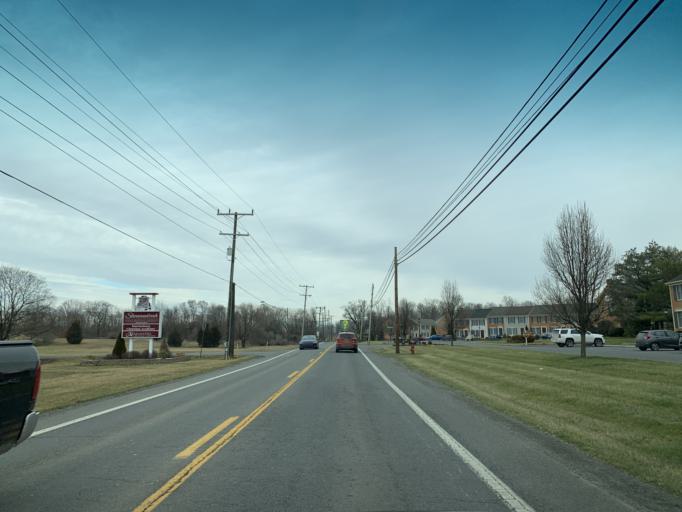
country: US
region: West Virginia
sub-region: Berkeley County
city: Martinsburg
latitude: 39.5031
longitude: -77.9376
